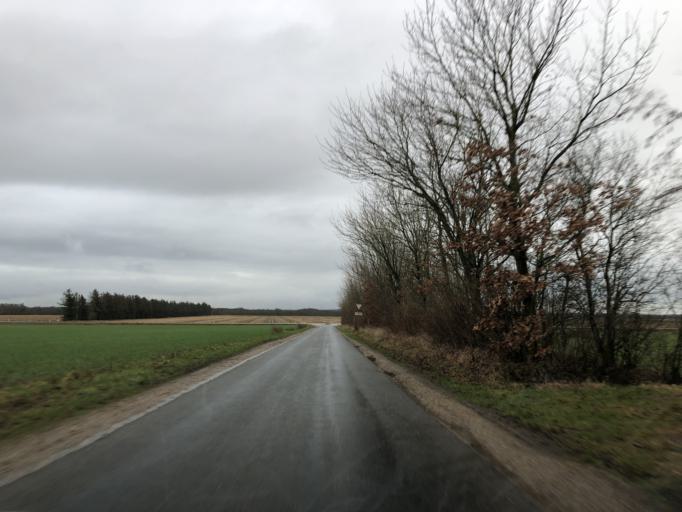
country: DK
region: Central Jutland
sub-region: Holstebro Kommune
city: Holstebro
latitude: 56.3726
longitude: 8.7290
